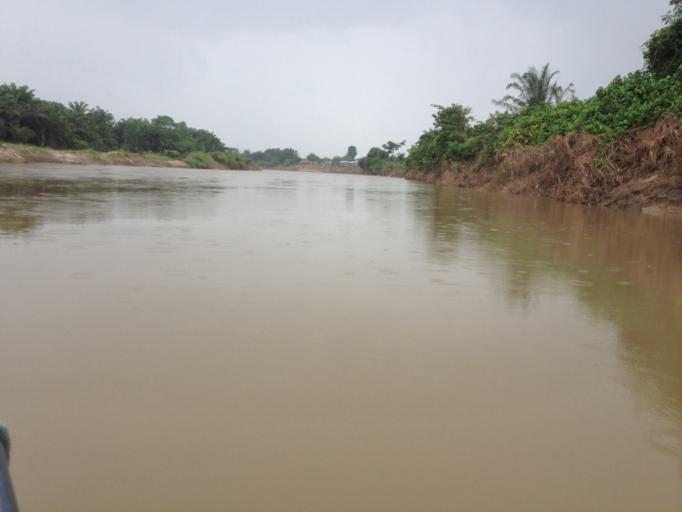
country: BJ
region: Mono
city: Lokossa
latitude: 6.5051
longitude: 1.6940
